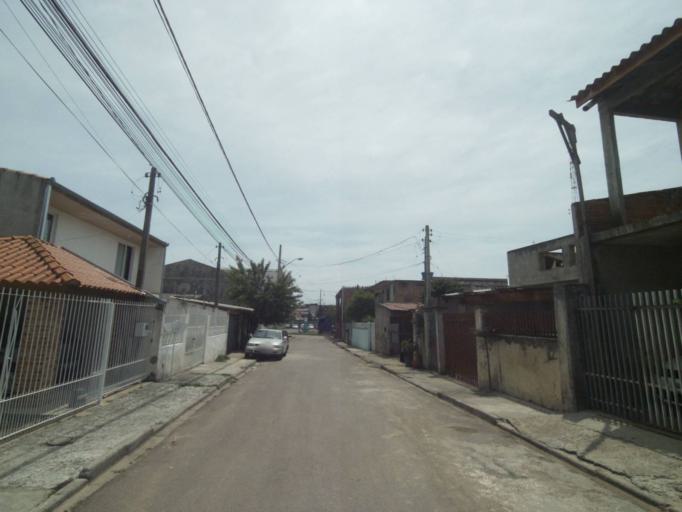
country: BR
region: Parana
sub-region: Curitiba
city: Curitiba
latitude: -25.4984
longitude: -49.3398
